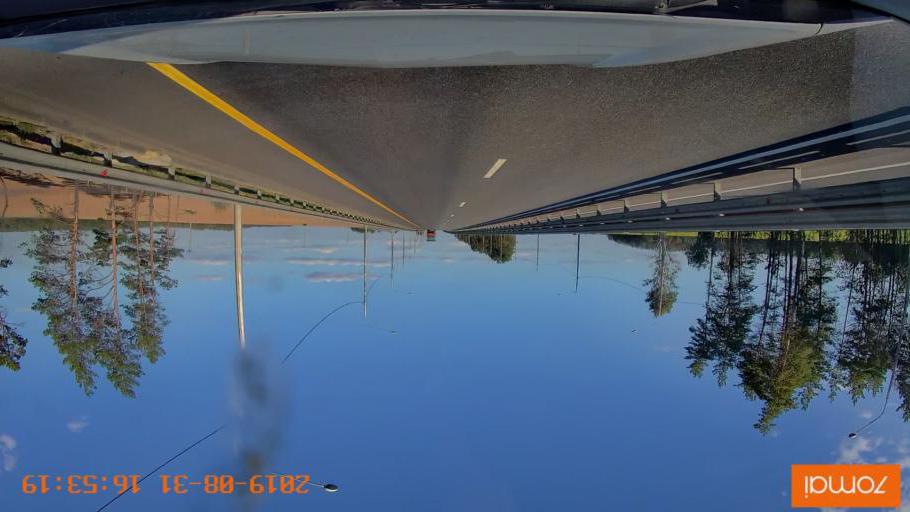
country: RU
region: Kaluga
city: Detchino
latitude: 54.7541
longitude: 36.2096
